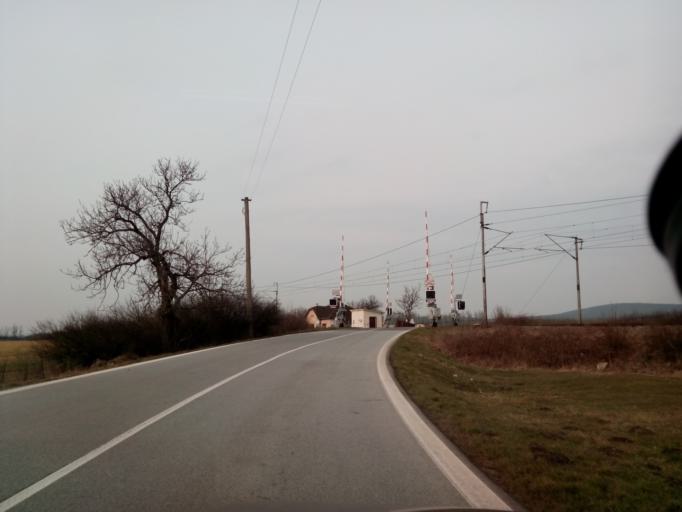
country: HU
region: Borsod-Abauj-Zemplen
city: Satoraljaujhely
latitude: 48.4678
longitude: 21.6388
